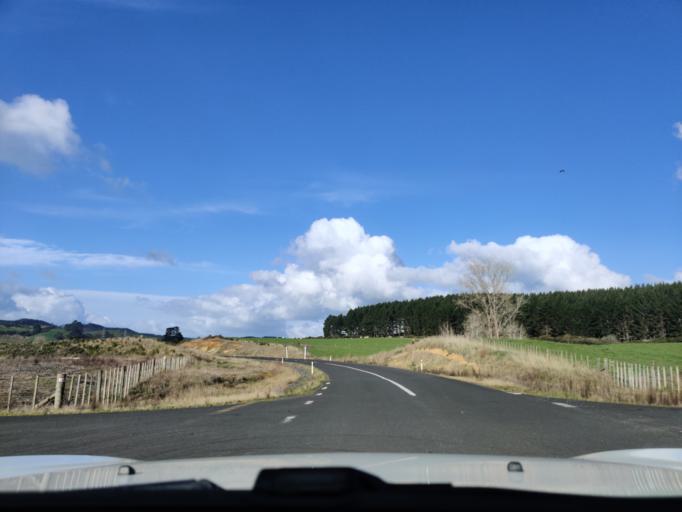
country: NZ
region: Waikato
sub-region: Waikato District
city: Te Kauwhata
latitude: -37.2827
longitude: 175.2001
